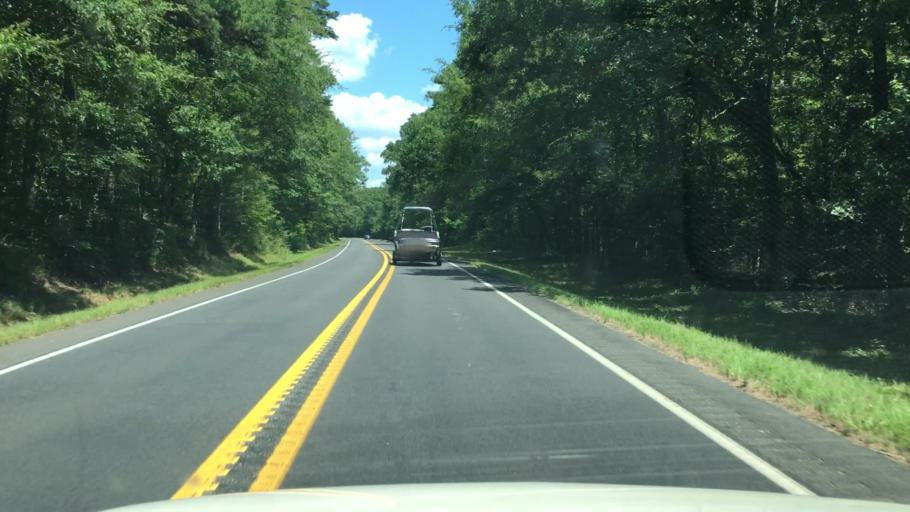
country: US
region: Arkansas
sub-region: Garland County
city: Lake Hamilton
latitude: 34.3602
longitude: -93.1743
